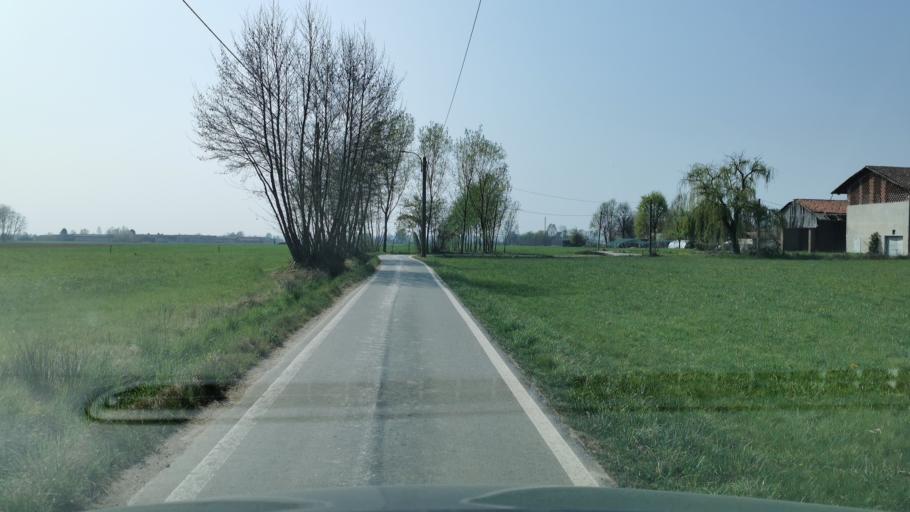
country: IT
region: Piedmont
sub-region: Provincia di Torino
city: Rivarolo Canavese
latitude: 45.3240
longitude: 7.7054
